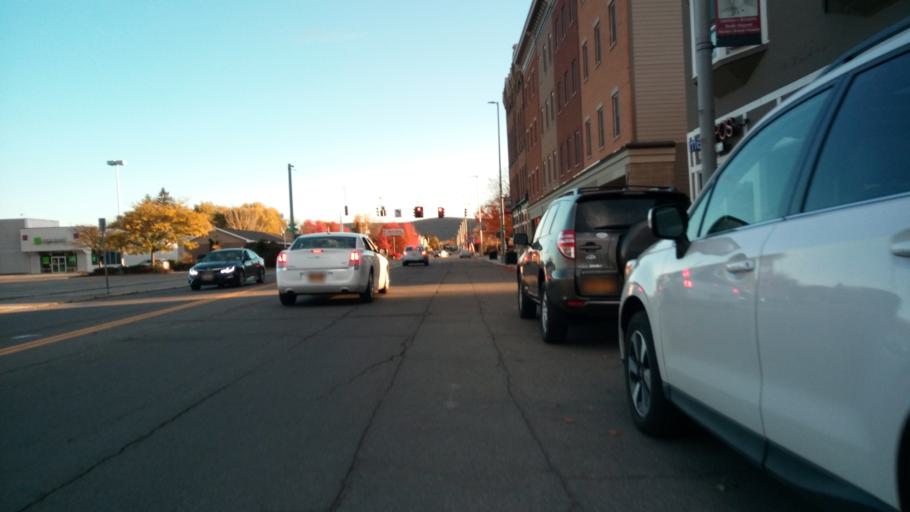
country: US
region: New York
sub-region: Chemung County
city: Elmira
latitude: 42.0832
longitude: -76.8053
